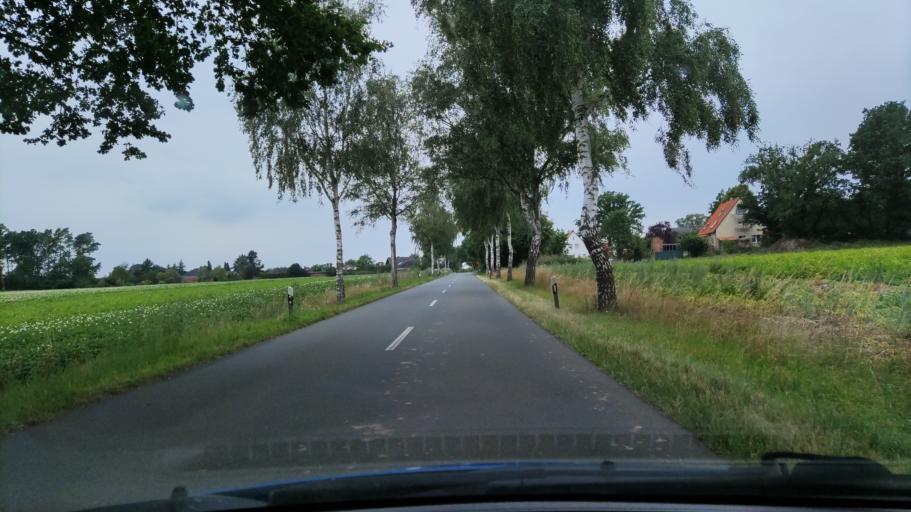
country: DE
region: Lower Saxony
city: Rosche
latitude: 52.9839
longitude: 10.7705
